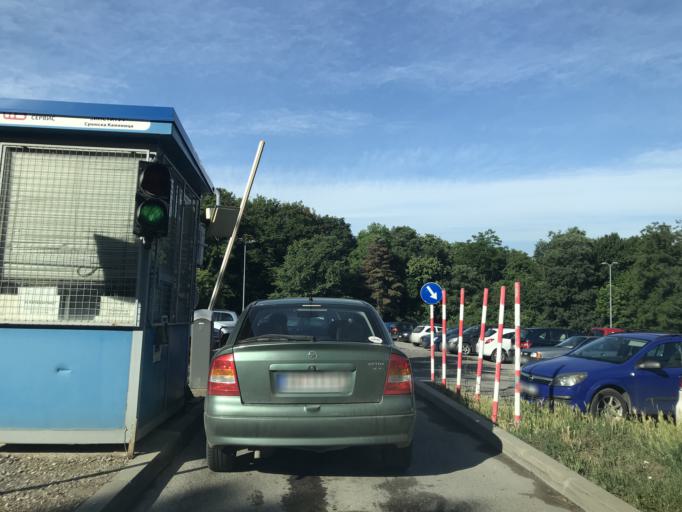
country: RS
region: Autonomna Pokrajina Vojvodina
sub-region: Juznobacki Okrug
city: Novi Sad
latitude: 45.2191
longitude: 19.8541
